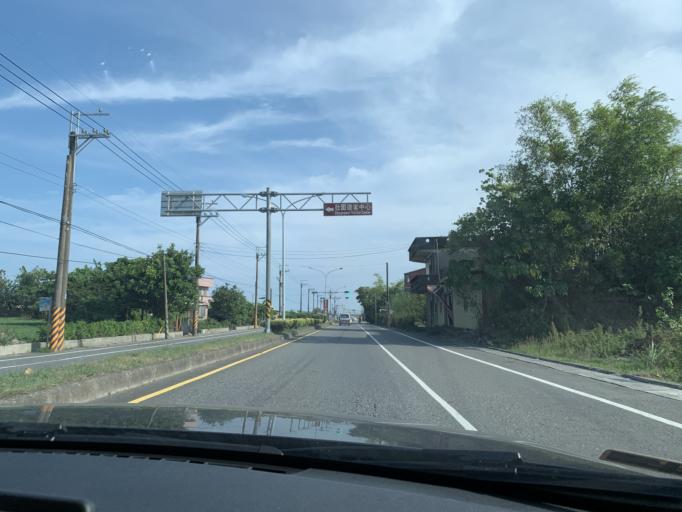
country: TW
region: Taiwan
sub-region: Yilan
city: Yilan
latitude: 24.7395
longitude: 121.8171
